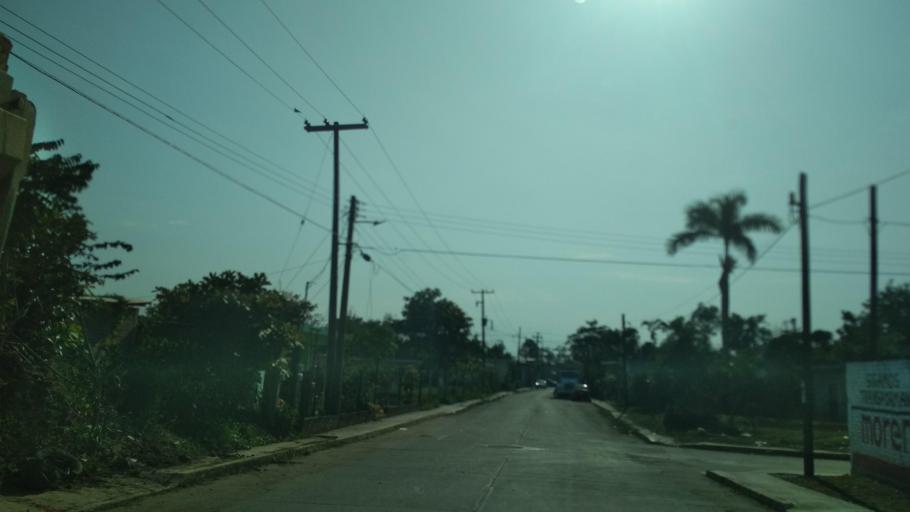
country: MM
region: Shan
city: Taunggyi
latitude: 20.3993
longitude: 97.3339
